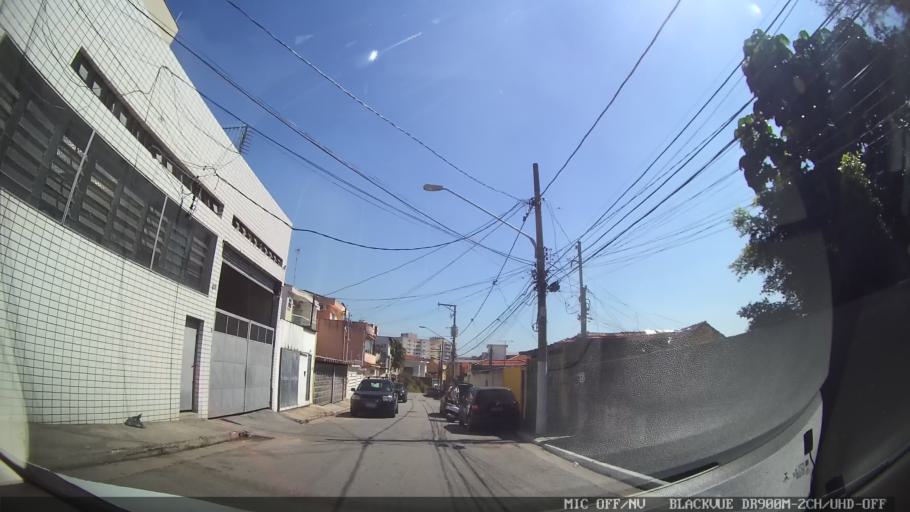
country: BR
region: Sao Paulo
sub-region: Sao Paulo
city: Sao Paulo
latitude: -23.5069
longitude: -46.6560
